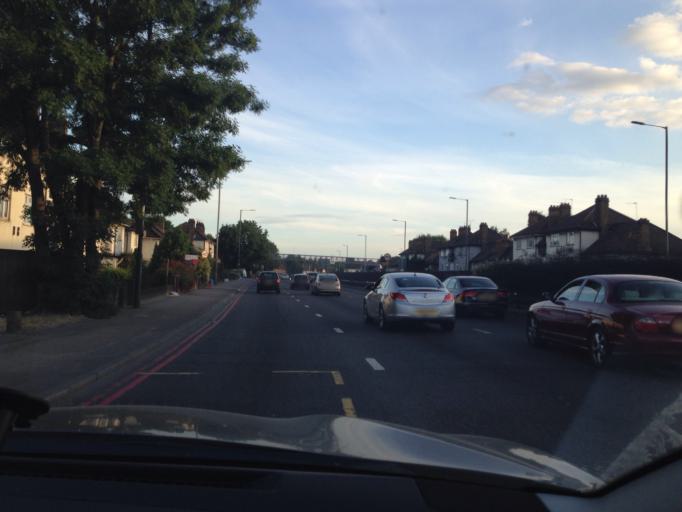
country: GB
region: England
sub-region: Greater London
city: Wembley
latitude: 51.5511
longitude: -0.2616
